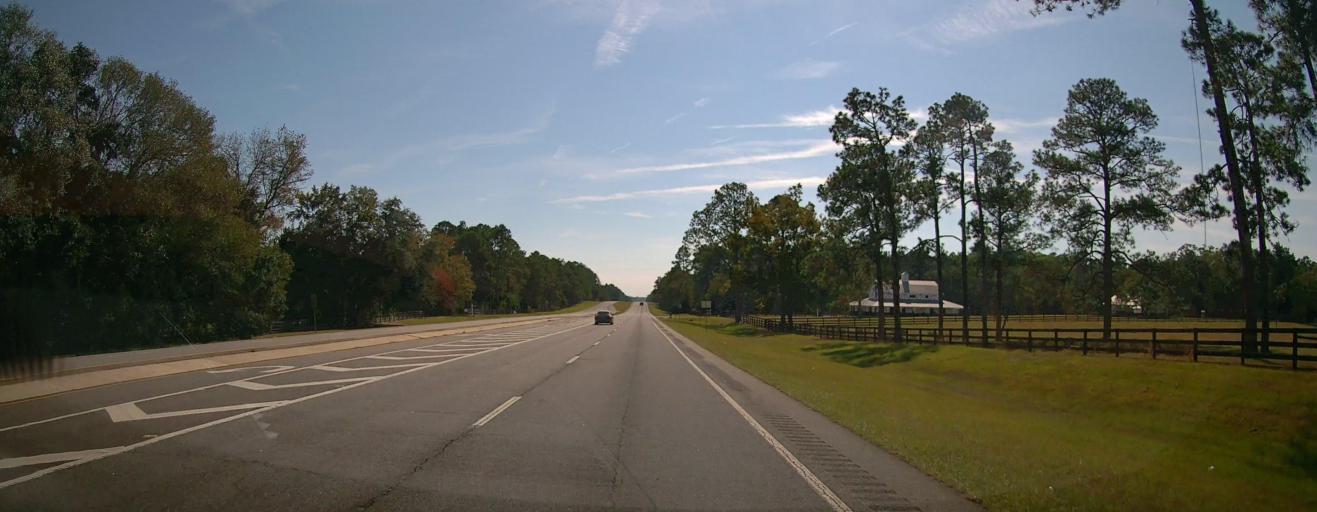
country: US
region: Georgia
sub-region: Lee County
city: Leesburg
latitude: 31.6935
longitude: -83.9926
